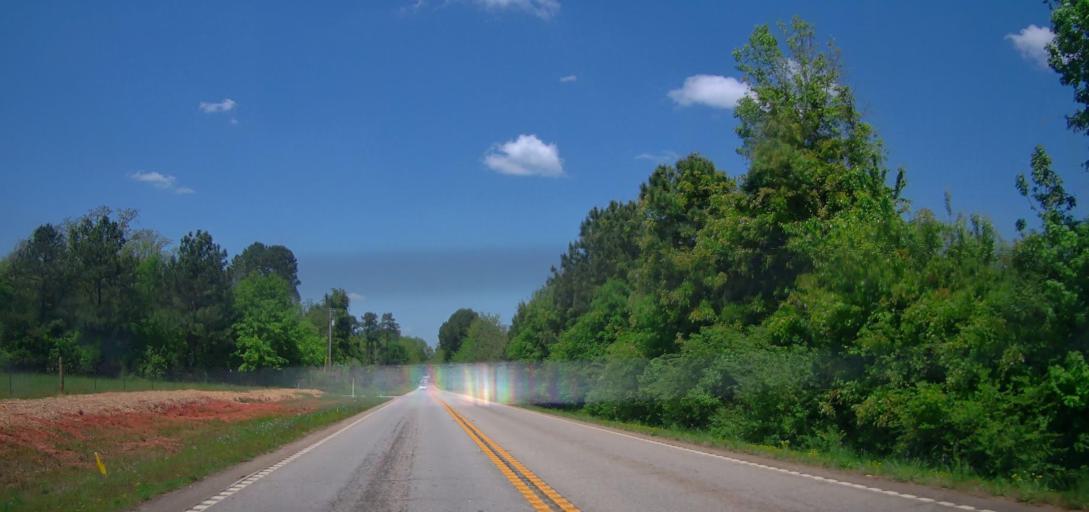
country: US
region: Georgia
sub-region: Jasper County
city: Monticello
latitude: 33.2892
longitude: -83.6770
